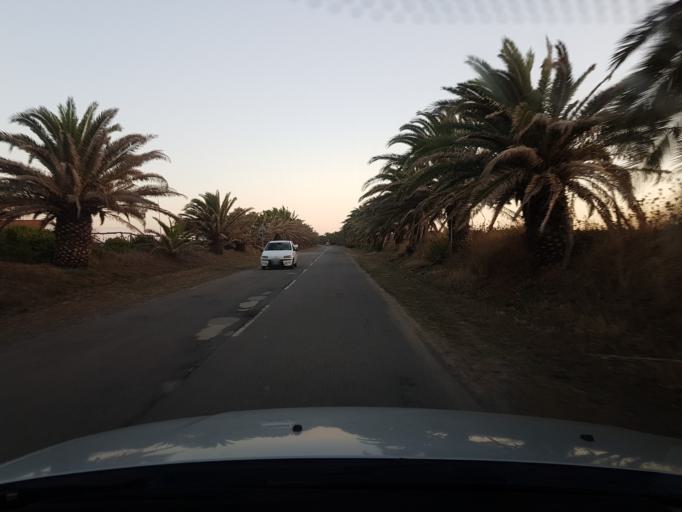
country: IT
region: Sardinia
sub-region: Provincia di Oristano
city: Riola Sardo
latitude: 40.0399
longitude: 8.4013
